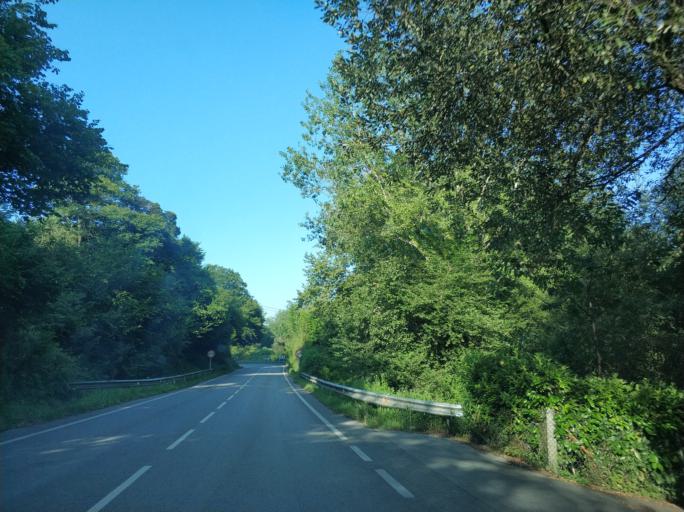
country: ES
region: Cantabria
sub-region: Provincia de Cantabria
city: Camargo
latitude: 43.3972
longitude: -3.9439
